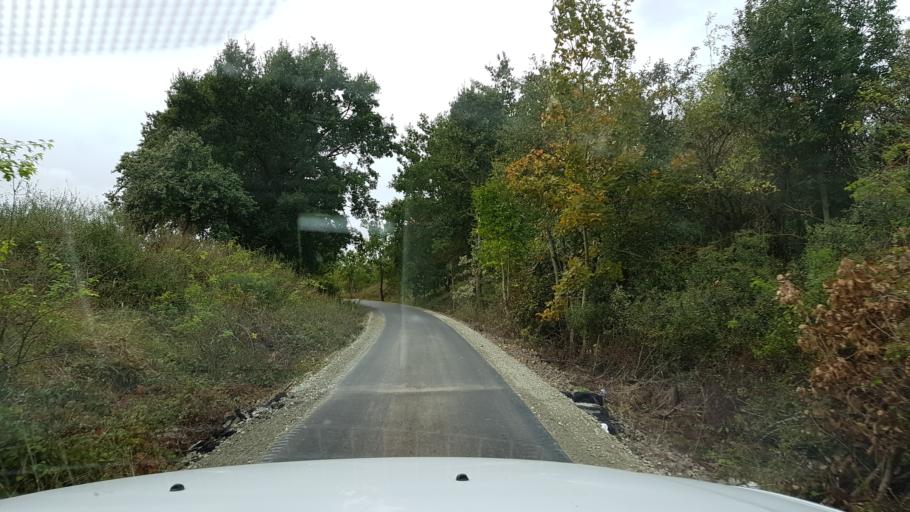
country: PL
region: West Pomeranian Voivodeship
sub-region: Powiat gryfinski
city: Moryn
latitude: 52.8747
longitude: 14.3825
